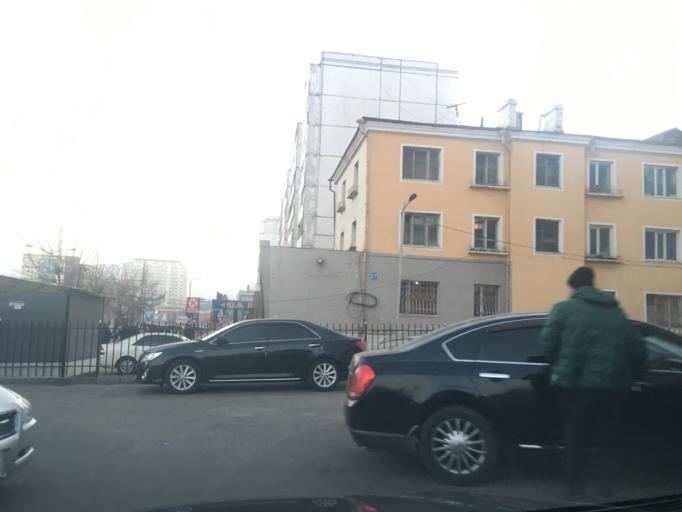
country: MN
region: Ulaanbaatar
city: Ulaanbaatar
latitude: 47.9208
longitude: 106.8903
